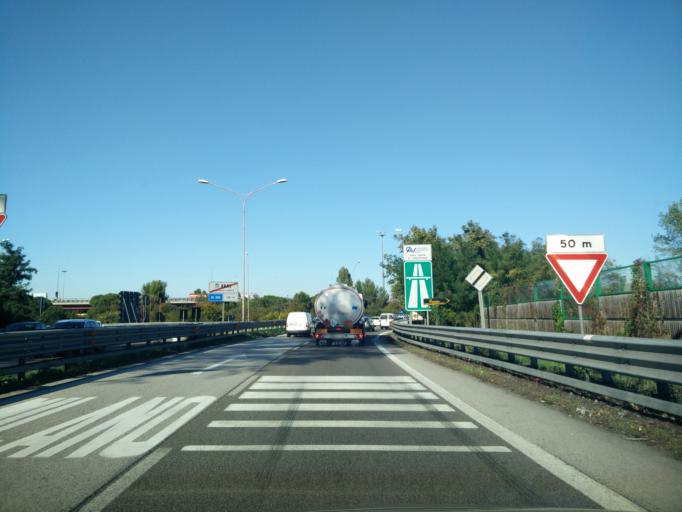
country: IT
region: Veneto
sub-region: Provincia di Venezia
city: Mestre
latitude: 45.4726
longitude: 12.2133
